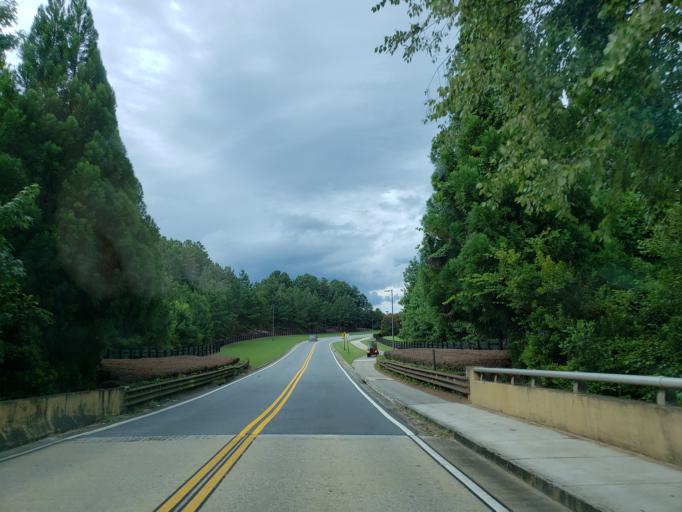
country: US
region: Georgia
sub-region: Bartow County
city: Emerson
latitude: 34.0218
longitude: -84.7844
